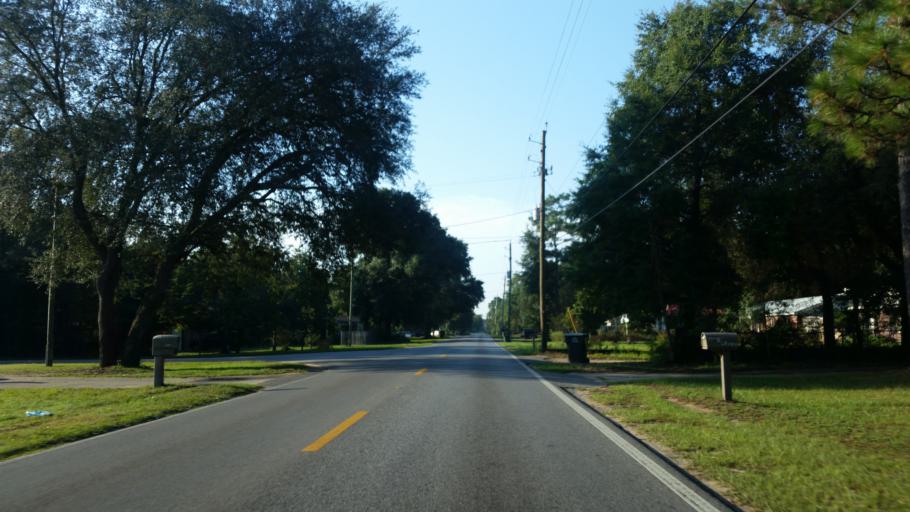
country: US
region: Florida
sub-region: Santa Rosa County
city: Bagdad
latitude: 30.5917
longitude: -87.0652
